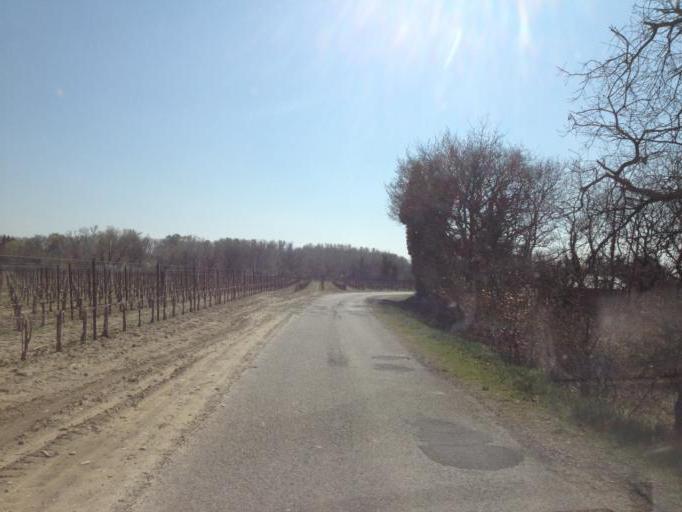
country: FR
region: Provence-Alpes-Cote d'Azur
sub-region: Departement du Vaucluse
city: Jonquieres
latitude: 44.0928
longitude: 4.9212
